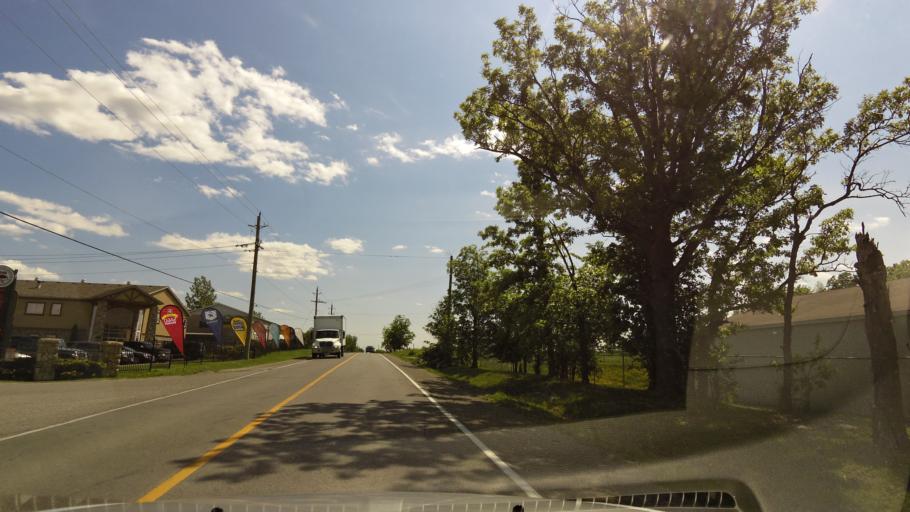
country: CA
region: Ontario
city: Brantford
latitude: 43.0897
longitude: -80.1044
